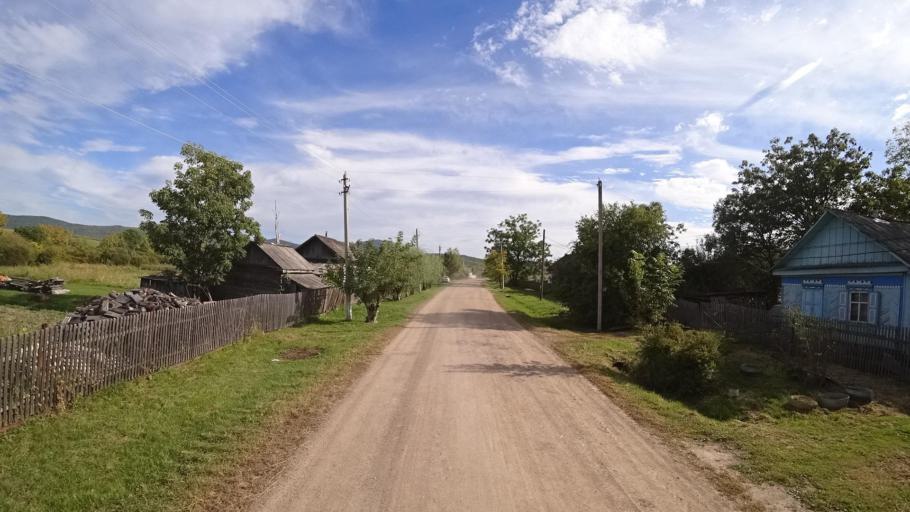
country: RU
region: Primorskiy
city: Dostoyevka
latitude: 44.3004
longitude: 133.4595
